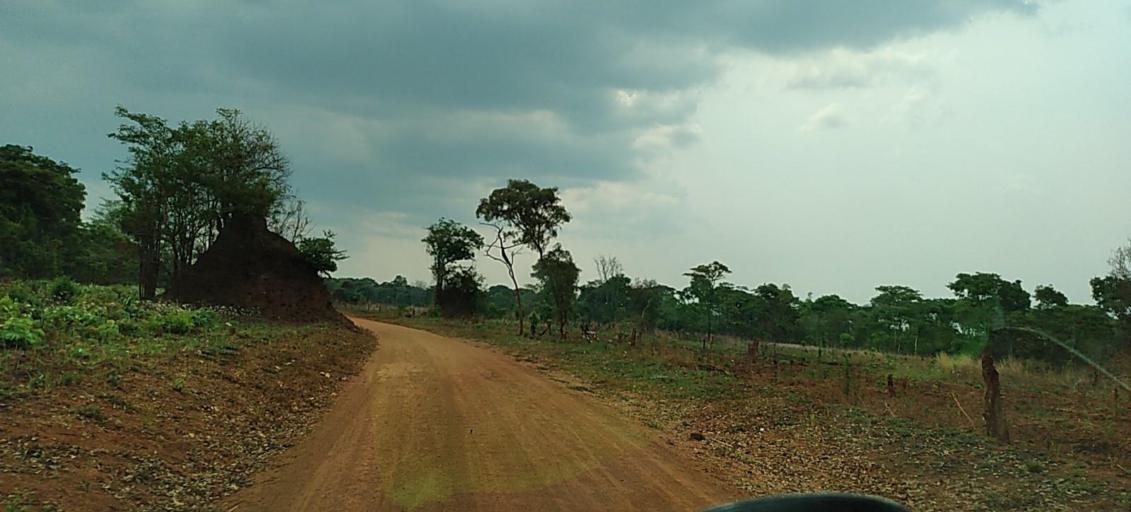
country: ZM
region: North-Western
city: Solwezi
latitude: -12.7825
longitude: 26.4971
